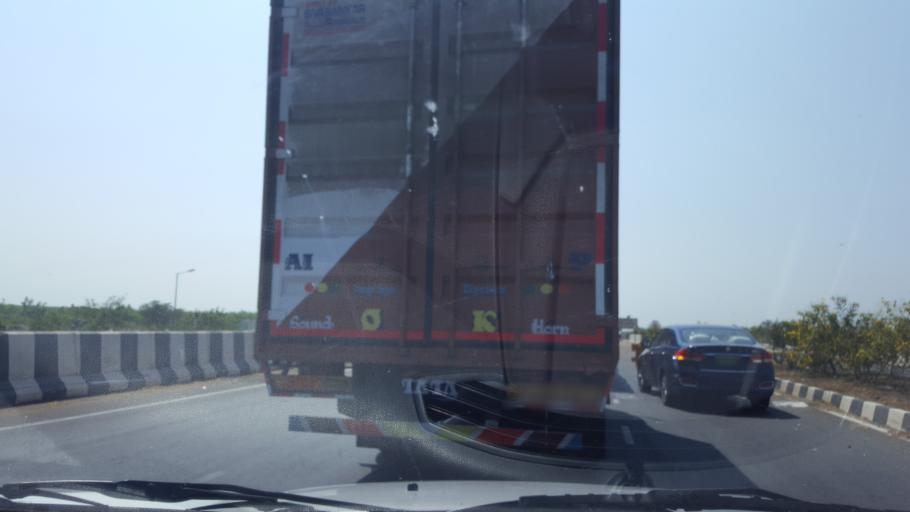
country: IN
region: Andhra Pradesh
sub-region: Prakasam
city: Addanki
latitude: 15.8051
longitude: 80.0408
